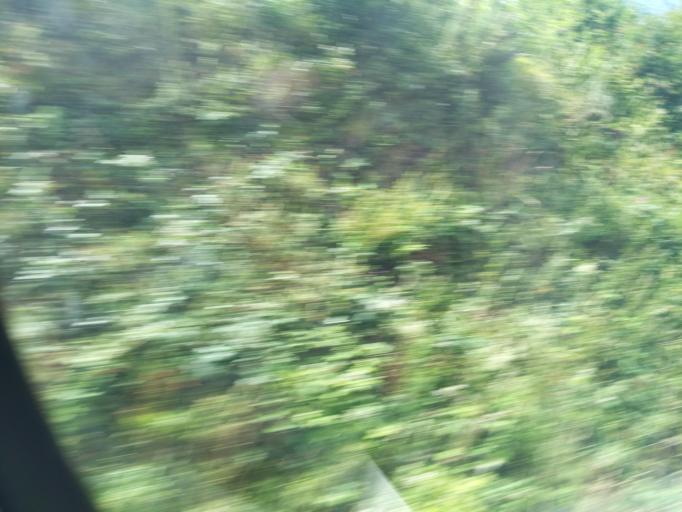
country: GB
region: England
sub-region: Cornwall
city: Pillaton
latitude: 50.4000
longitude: -4.3440
